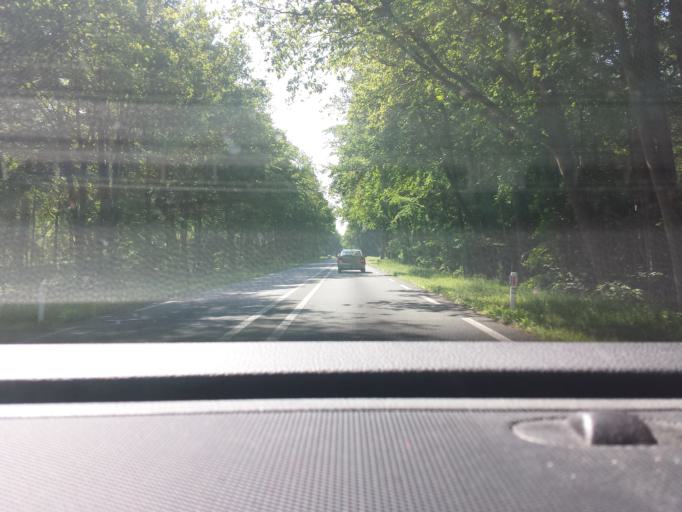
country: NL
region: Gelderland
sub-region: Gemeente Lochem
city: Almen
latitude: 52.1416
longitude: 6.3423
